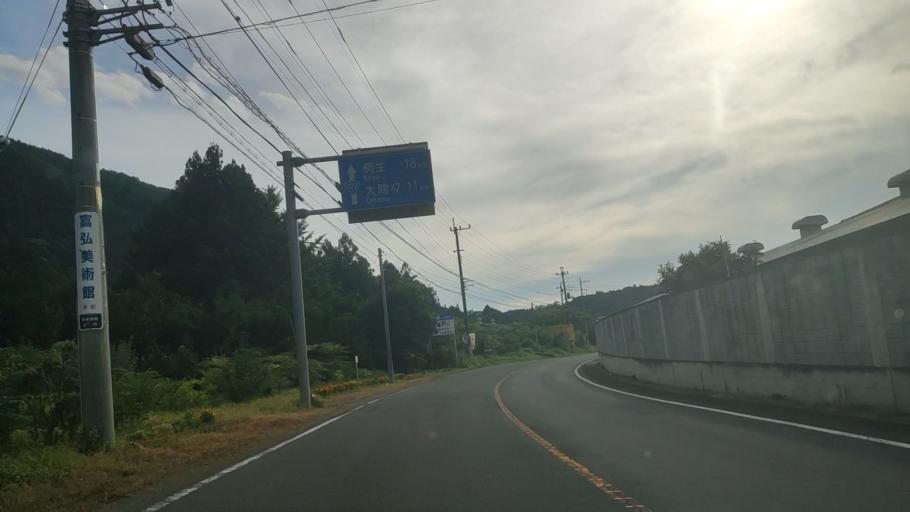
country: JP
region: Gunma
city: Omamacho-omama
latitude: 36.5014
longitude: 139.2905
